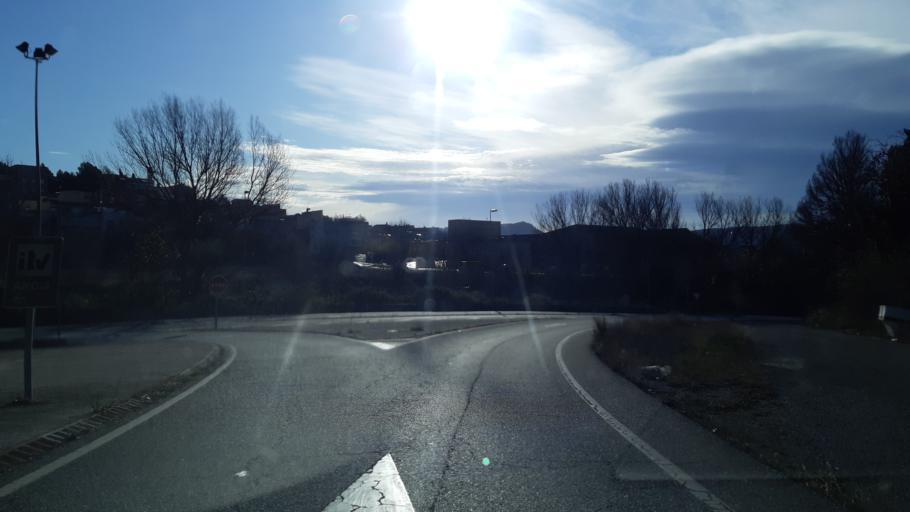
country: ES
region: Catalonia
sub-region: Provincia de Barcelona
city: Vilanova del Cami
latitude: 41.5832
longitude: 1.6353
